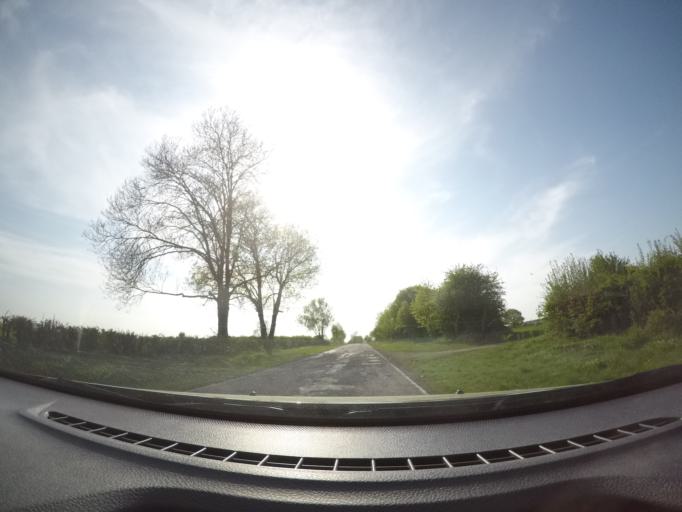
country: BE
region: Wallonia
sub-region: Province du Luxembourg
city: Tintigny
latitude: 49.6640
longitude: 5.5038
